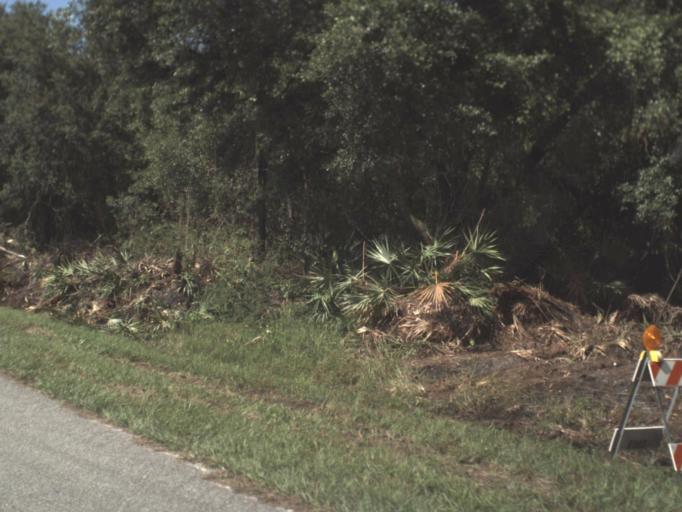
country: US
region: Florida
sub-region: Sarasota County
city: Lake Sarasota
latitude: 27.3679
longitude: -82.2115
